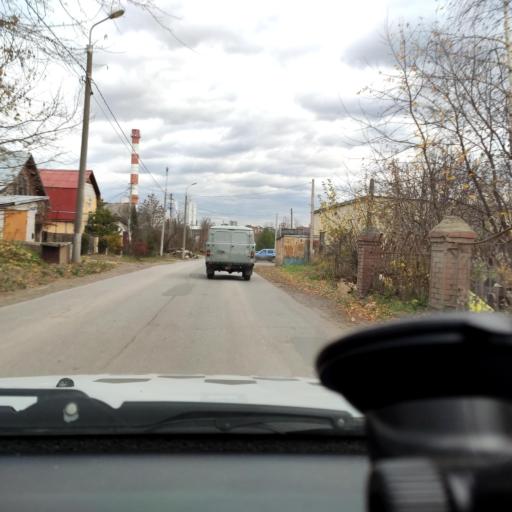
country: RU
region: Perm
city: Perm
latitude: 57.9960
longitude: 56.3130
